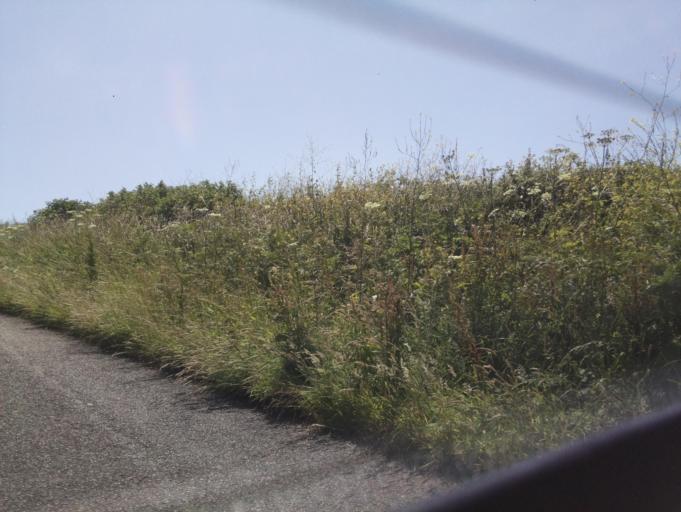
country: GB
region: England
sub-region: Devon
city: Dartmouth
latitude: 50.3863
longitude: -3.5612
